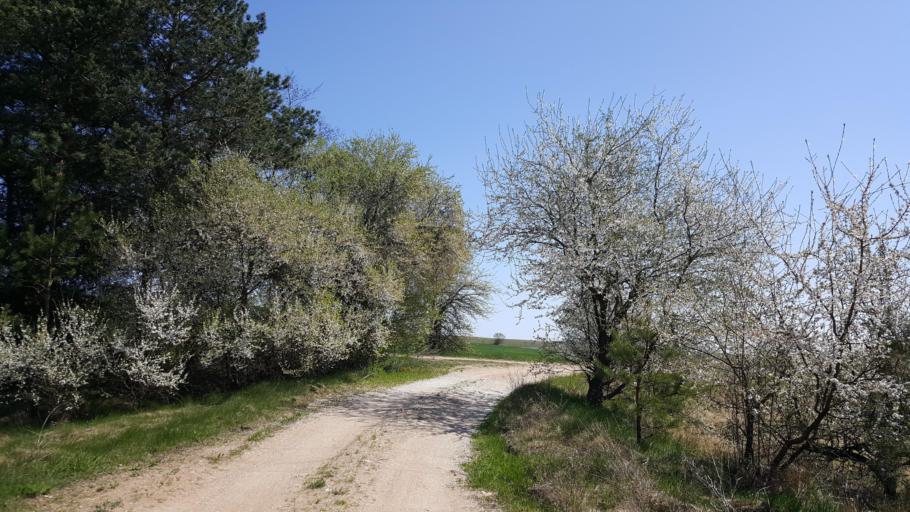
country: BY
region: Brest
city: Charnawchytsy
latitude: 52.3292
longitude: 23.6953
